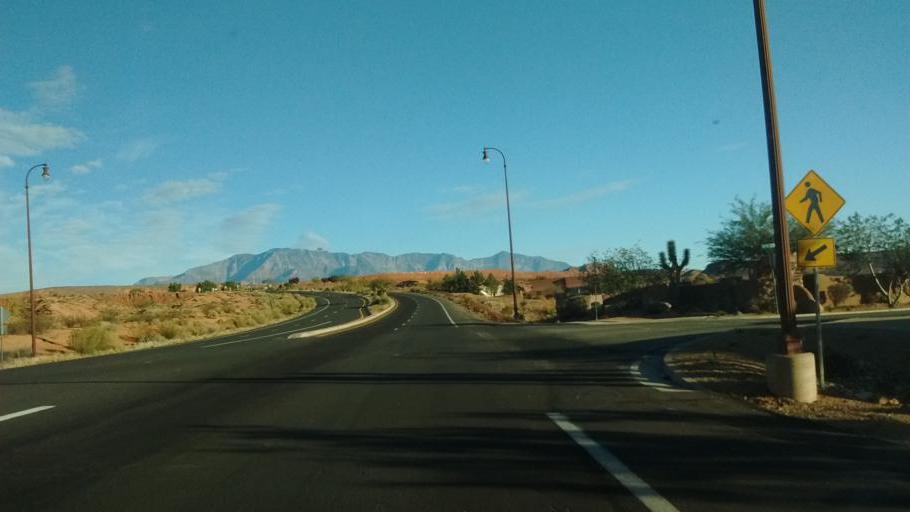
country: US
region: Utah
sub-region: Washington County
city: Washington
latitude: 37.1405
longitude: -113.4853
